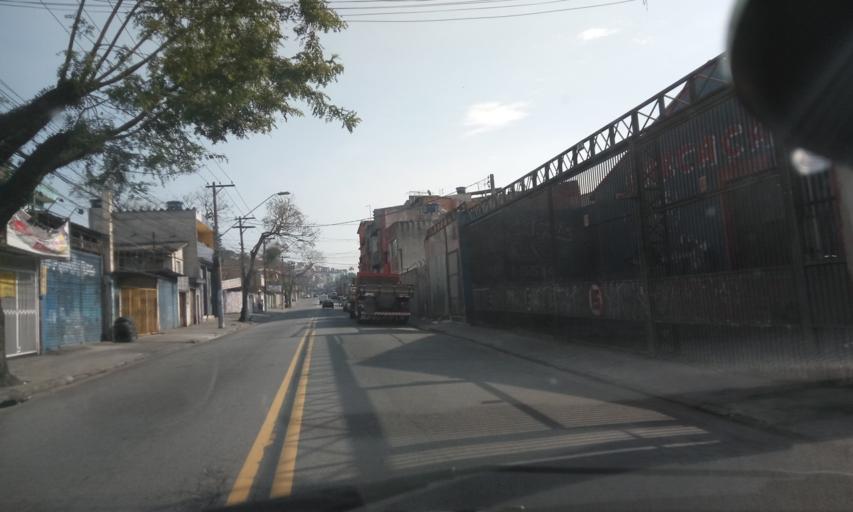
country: BR
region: Sao Paulo
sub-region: Santo Andre
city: Santo Andre
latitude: -23.7000
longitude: -46.5093
